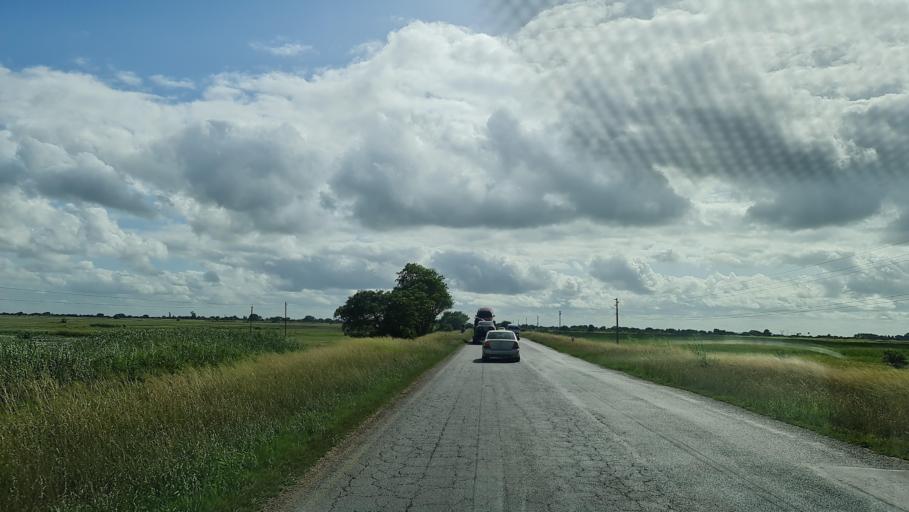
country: MZ
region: Gaza
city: Macia
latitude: -25.0967
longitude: 32.8300
